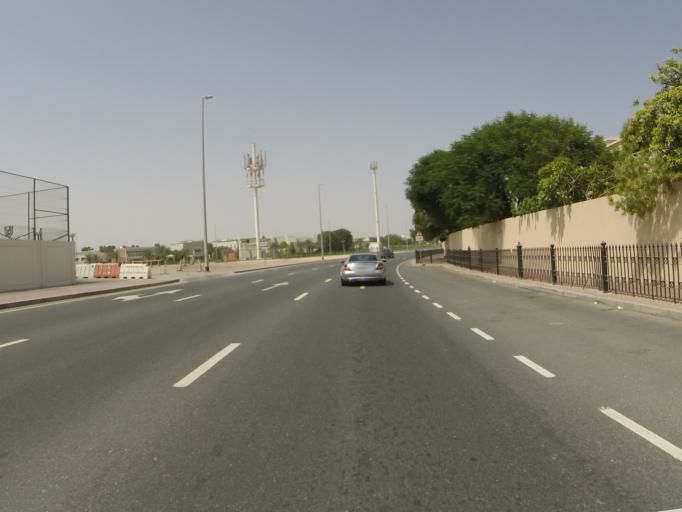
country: AE
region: Dubai
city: Dubai
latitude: 25.0779
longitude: 55.1778
